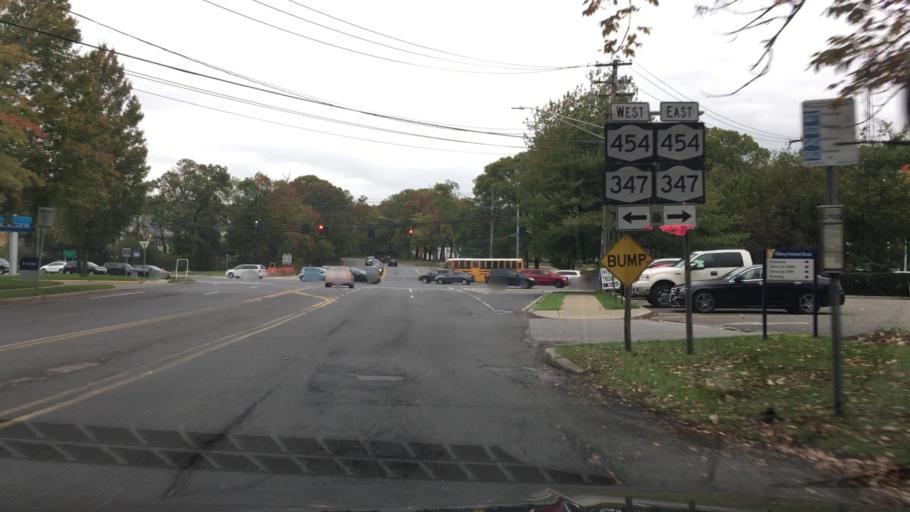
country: US
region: New York
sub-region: Suffolk County
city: Hauppauge
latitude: 40.8244
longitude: -73.2345
